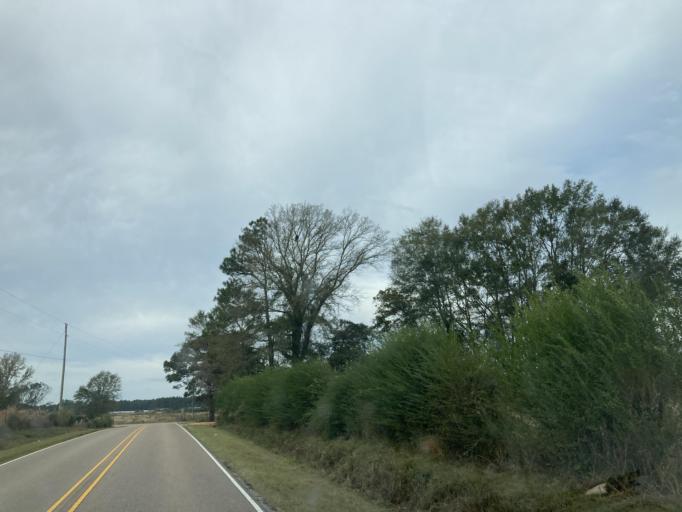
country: US
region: Mississippi
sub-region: Lamar County
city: Purvis
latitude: 31.1237
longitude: -89.4796
